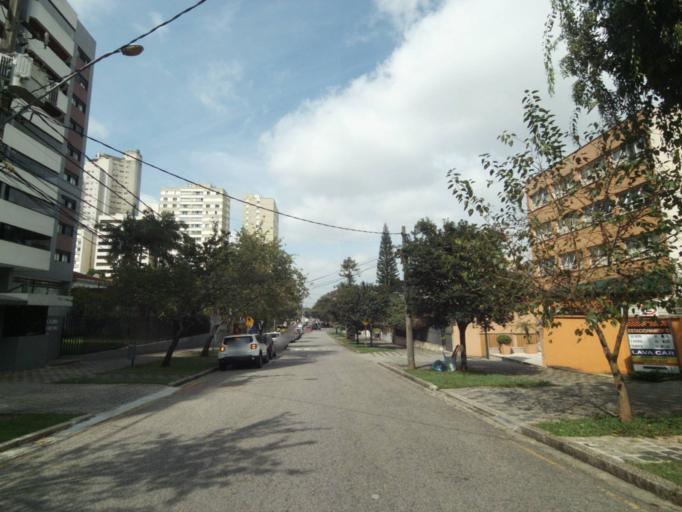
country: BR
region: Parana
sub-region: Curitiba
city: Curitiba
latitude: -25.4318
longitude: -49.2589
